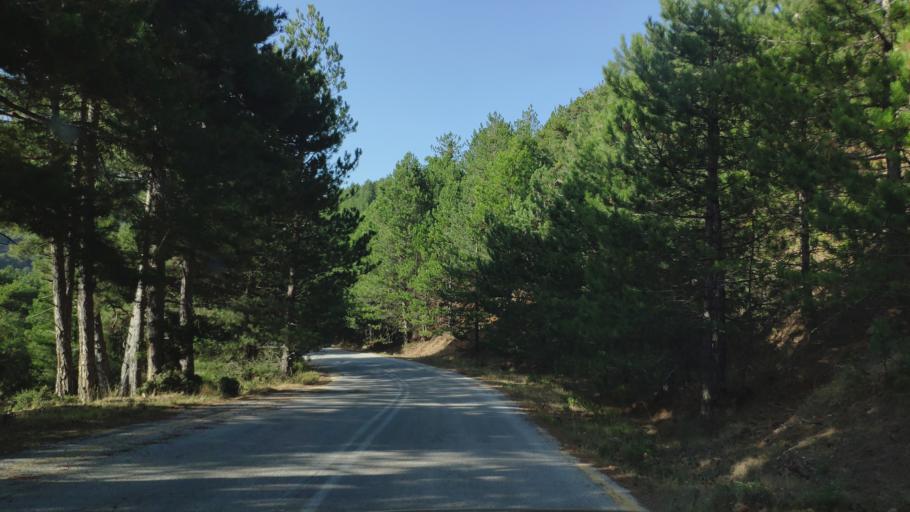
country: GR
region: West Greece
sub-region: Nomos Achaias
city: Aiyira
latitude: 38.0513
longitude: 22.3838
